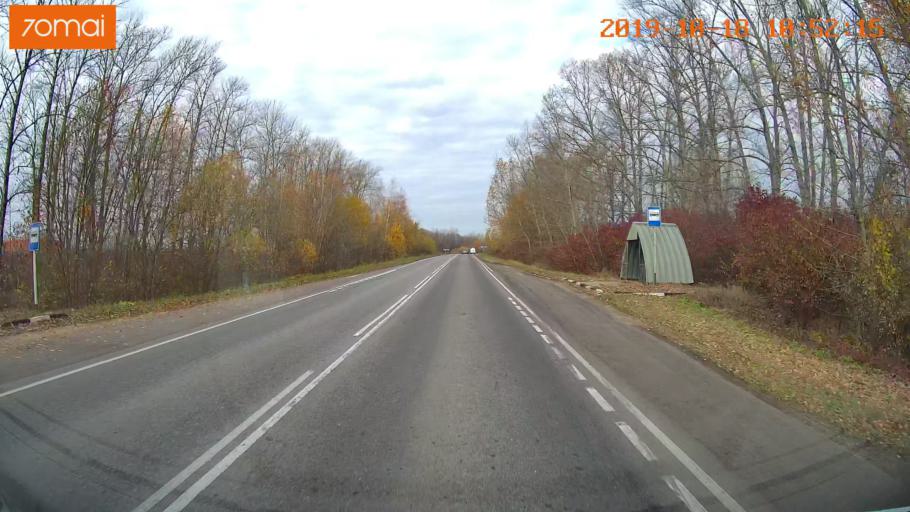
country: RU
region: Tula
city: Yepifan'
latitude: 53.7642
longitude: 38.6544
